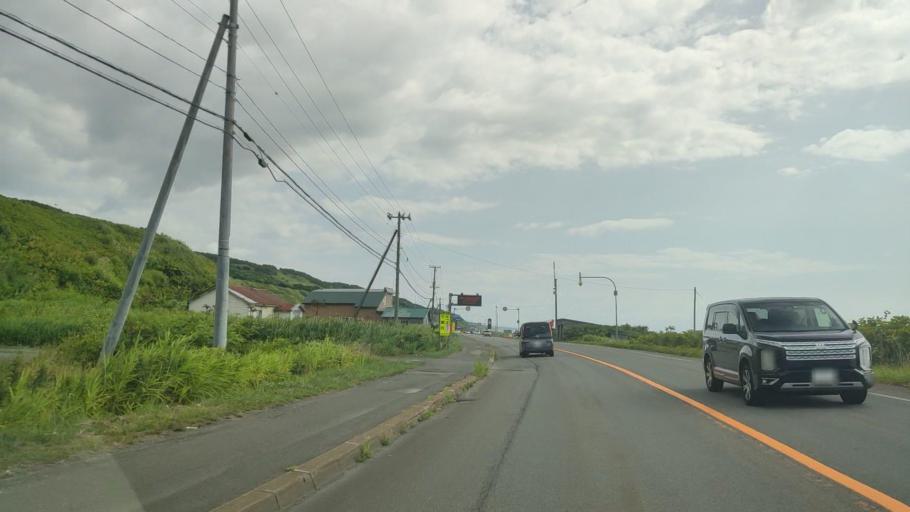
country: JP
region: Hokkaido
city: Rumoi
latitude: 44.1406
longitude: 141.6540
